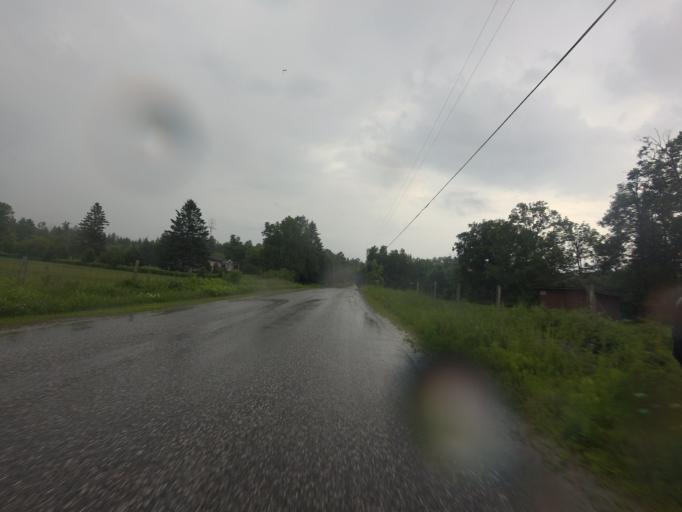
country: CA
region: Quebec
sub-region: Outaouais
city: Maniwaki
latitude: 46.4102
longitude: -75.9579
